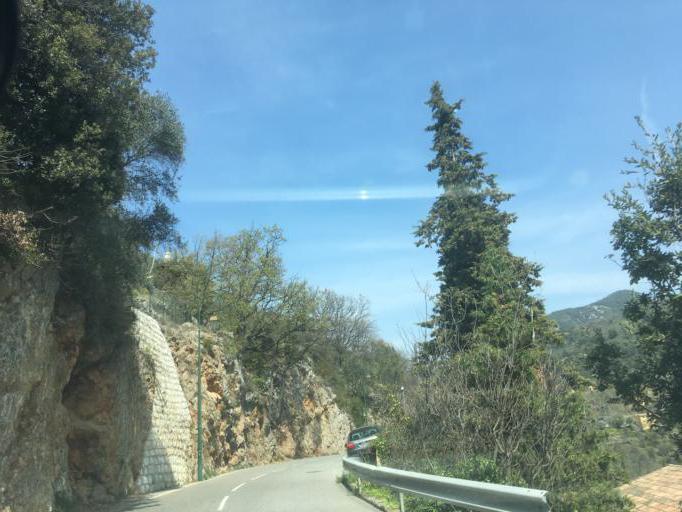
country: FR
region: Provence-Alpes-Cote d'Azur
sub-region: Departement des Alpes-Maritimes
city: Levens
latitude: 43.8520
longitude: 7.2268
